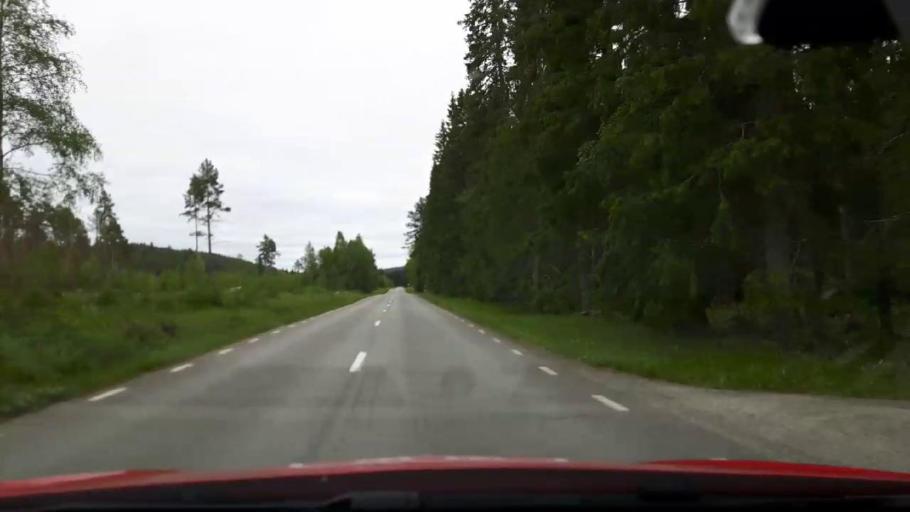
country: SE
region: Jaemtland
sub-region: Stroemsunds Kommun
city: Stroemsund
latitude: 63.4412
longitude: 15.4827
